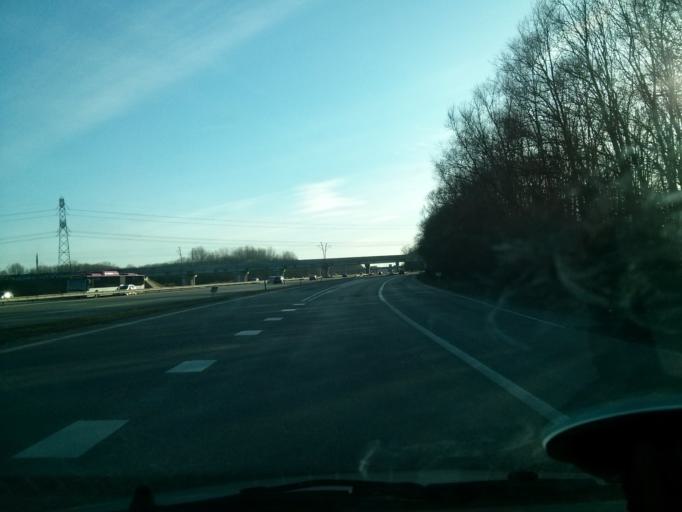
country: NL
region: Gelderland
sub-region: Gemeente Overbetuwe
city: Elst
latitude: 51.9027
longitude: 5.8713
